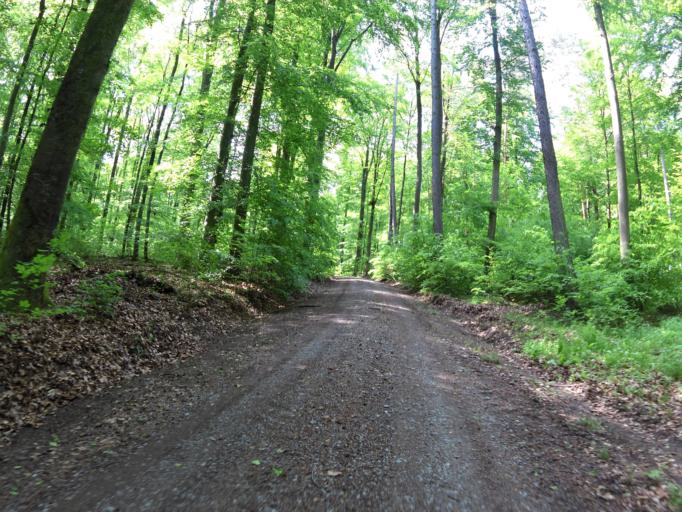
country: DE
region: Bavaria
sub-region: Regierungsbezirk Unterfranken
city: Wuerzburg
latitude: 49.7523
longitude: 9.8687
